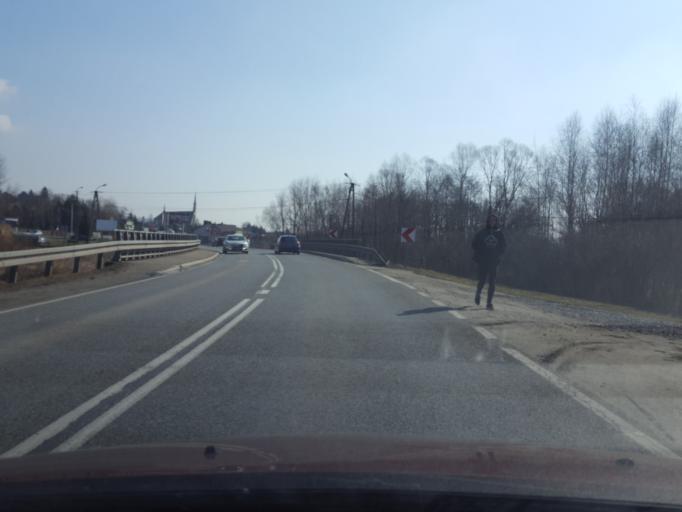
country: PL
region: Lesser Poland Voivodeship
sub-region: Powiat brzeski
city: Czchow
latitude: 49.8507
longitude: 20.6785
